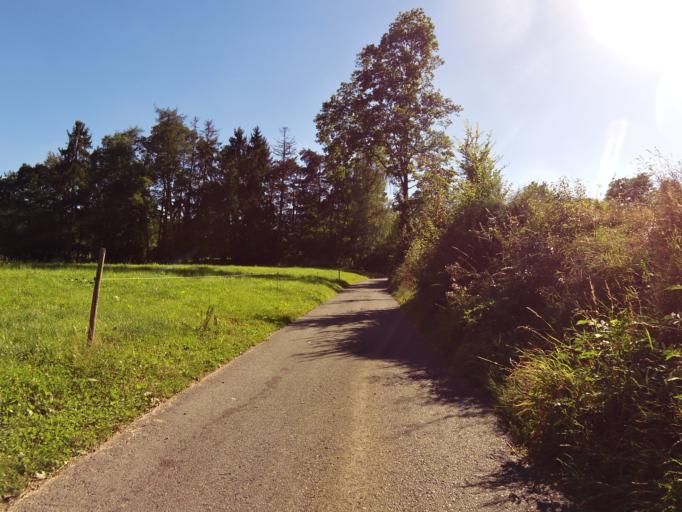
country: DE
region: Hesse
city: Reichelsheim
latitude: 49.6668
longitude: 8.8659
